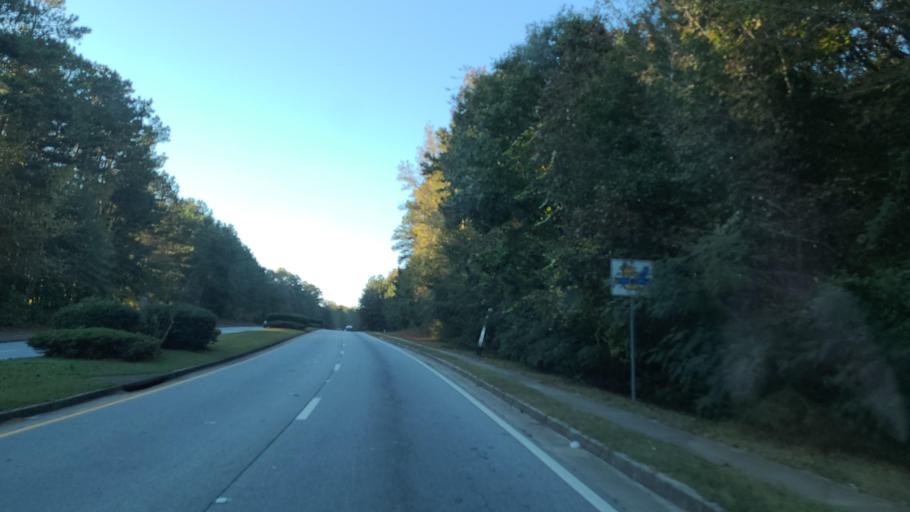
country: US
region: Georgia
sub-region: Clayton County
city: Jonesboro
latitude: 33.5320
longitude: -84.3376
